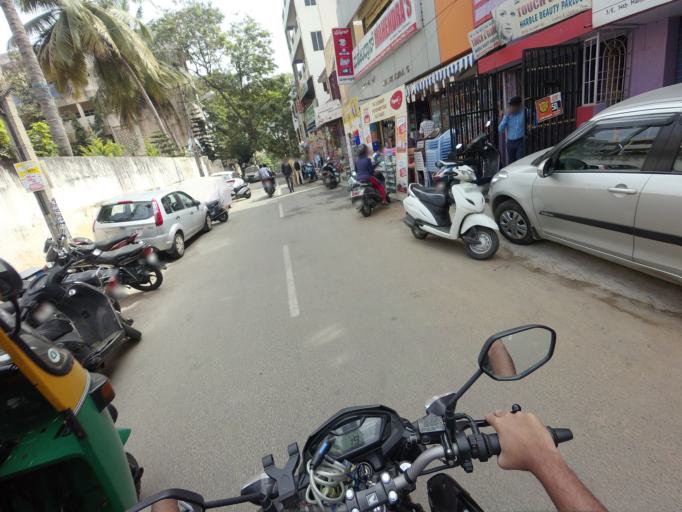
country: IN
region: Karnataka
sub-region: Bangalore Urban
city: Bangalore
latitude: 12.9702
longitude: 77.5378
